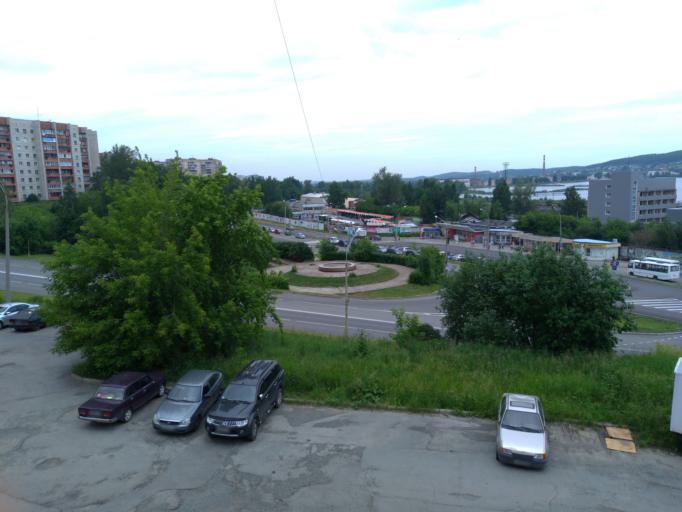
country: RU
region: Sverdlovsk
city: Verkh-Neyvinskiy
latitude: 57.2529
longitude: 60.1167
